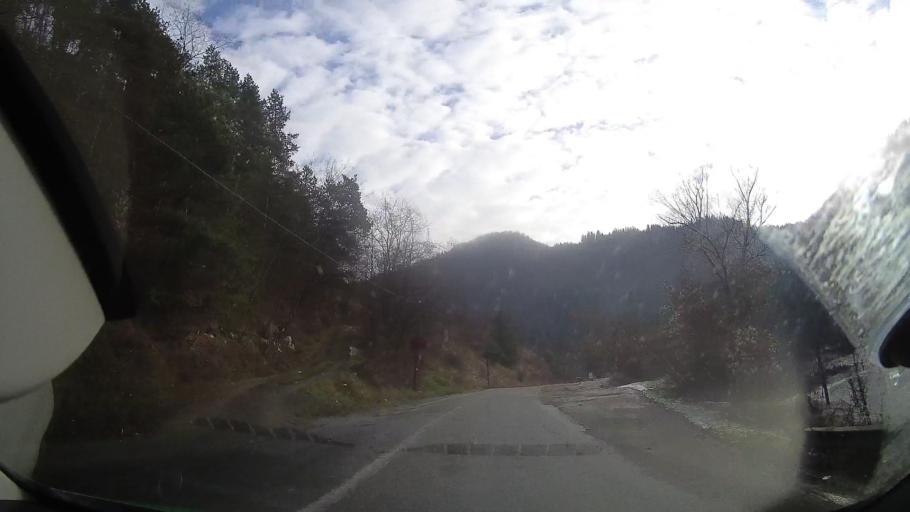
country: RO
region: Alba
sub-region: Comuna Bistra
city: Bistra
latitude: 46.3786
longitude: 23.1475
